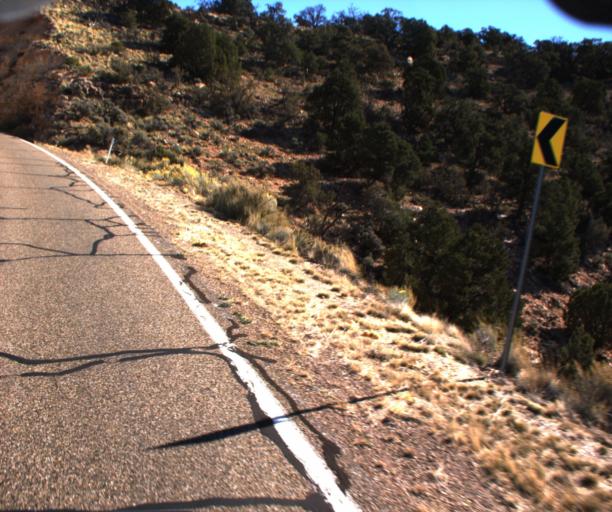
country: US
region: Arizona
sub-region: Coconino County
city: Fredonia
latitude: 36.8465
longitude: -112.2608
